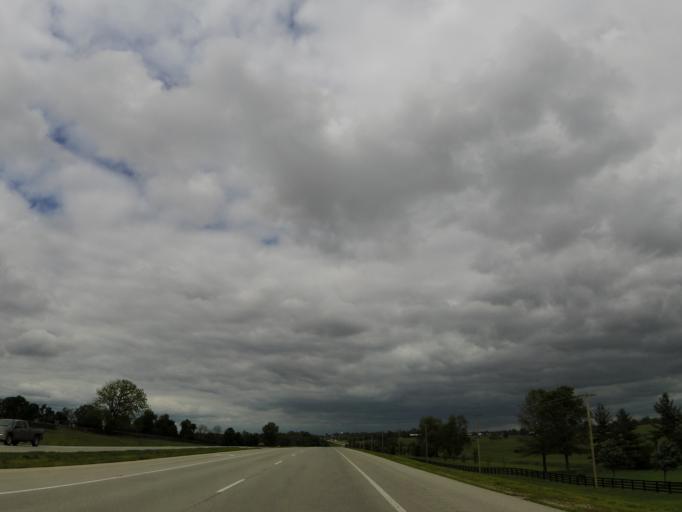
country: US
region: Kentucky
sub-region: Scott County
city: Georgetown
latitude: 38.1819
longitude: -84.5933
